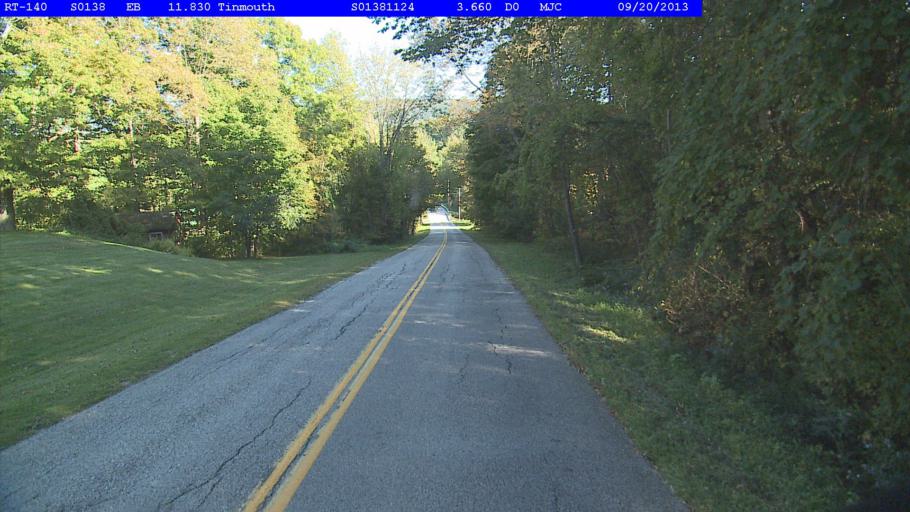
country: US
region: Vermont
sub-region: Rutland County
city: West Rutland
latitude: 43.4506
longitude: -73.0437
